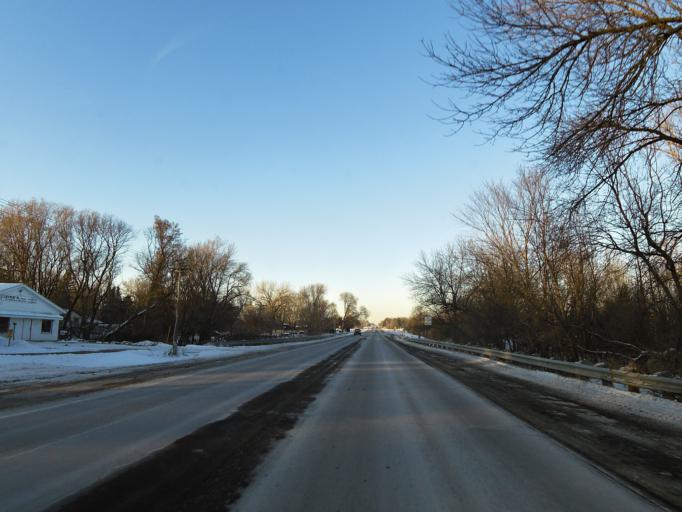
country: US
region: Minnesota
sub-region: Dakota County
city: Farmington
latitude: 44.6537
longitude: -93.1367
